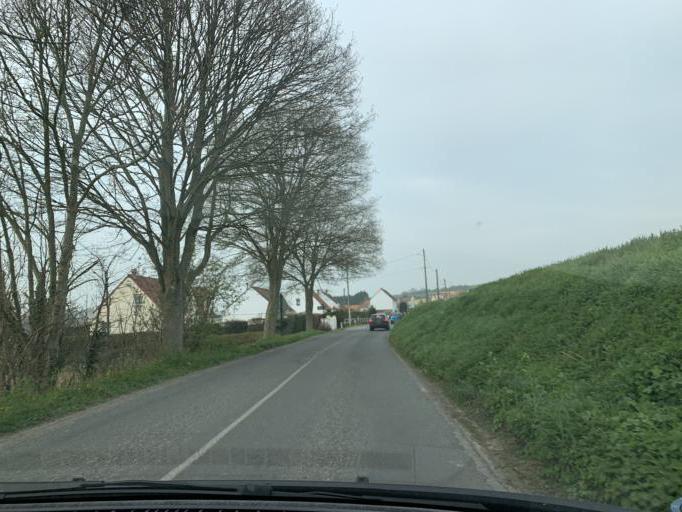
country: FR
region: Nord-Pas-de-Calais
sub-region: Departement du Pas-de-Calais
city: Montreuil
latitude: 50.4959
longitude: 1.7911
